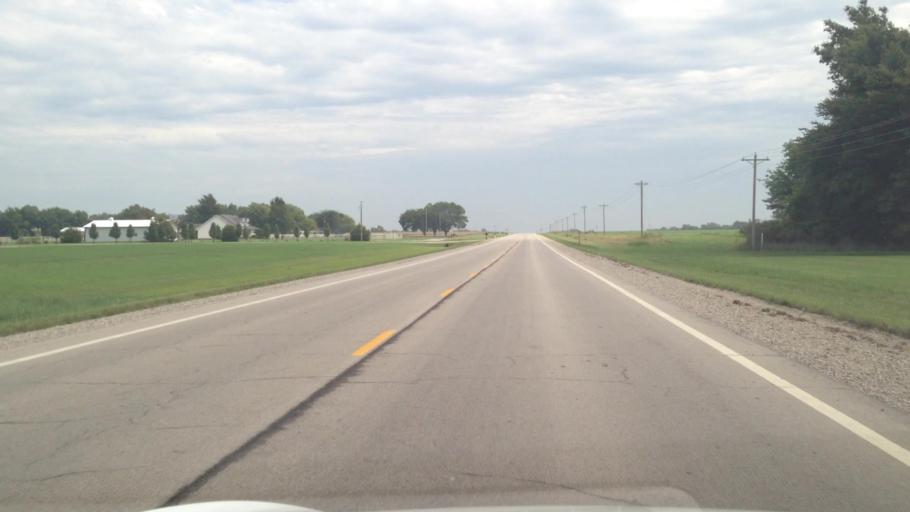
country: US
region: Kansas
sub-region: Crawford County
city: Girard
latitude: 37.5144
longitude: -94.9342
